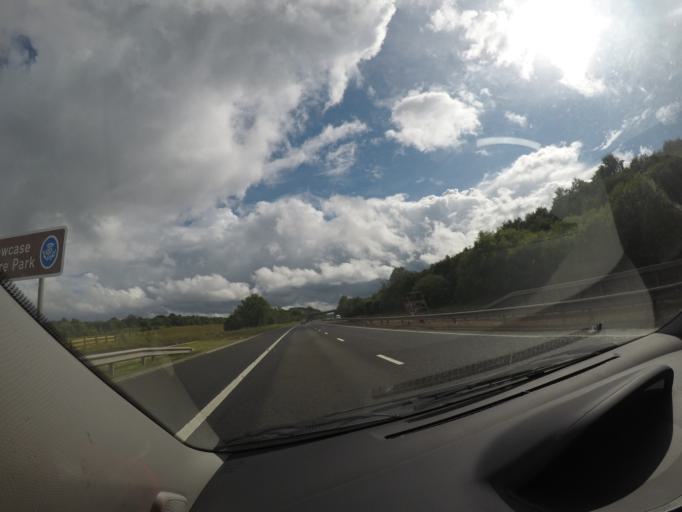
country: GB
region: Scotland
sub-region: North Lanarkshire
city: Glenboig
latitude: 55.8699
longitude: -4.0792
